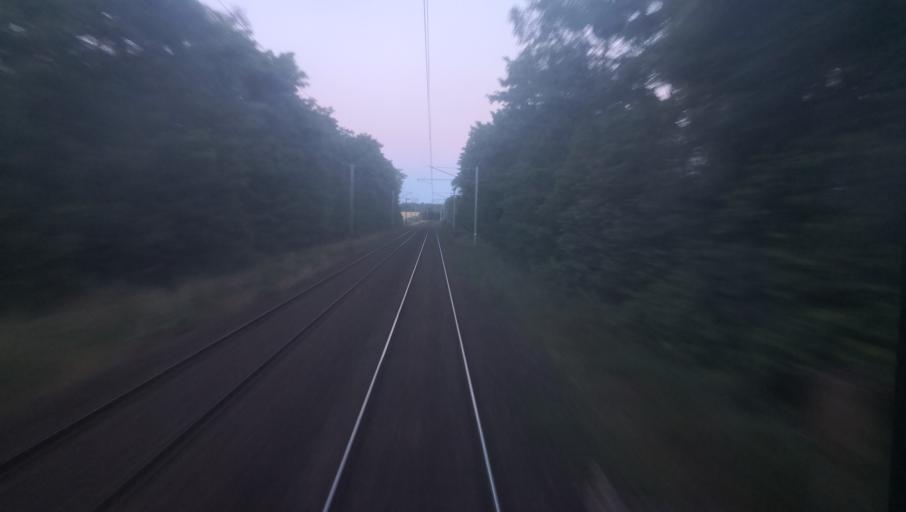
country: FR
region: Centre
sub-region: Departement du Loiret
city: Saint-Martin-sur-Ocre
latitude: 47.6816
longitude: 2.6674
